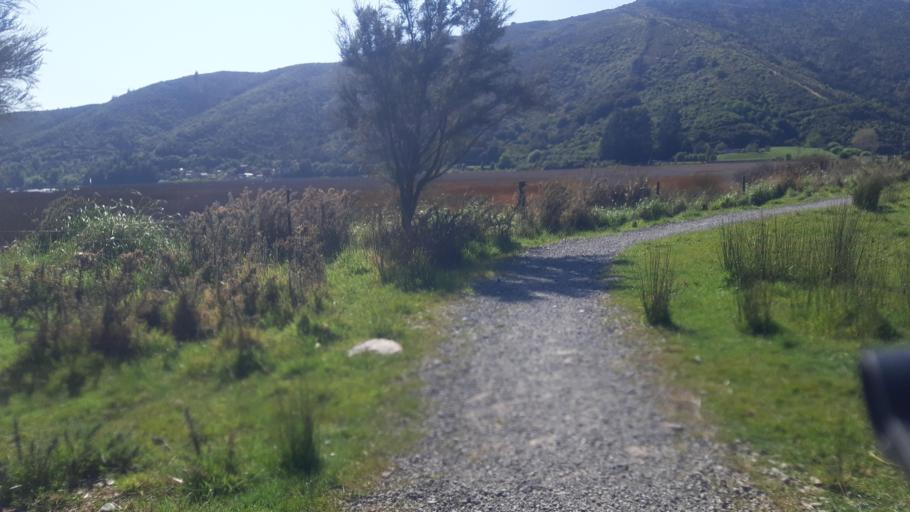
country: NZ
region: Marlborough
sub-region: Marlborough District
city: Picton
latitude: -41.2849
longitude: 173.7695
